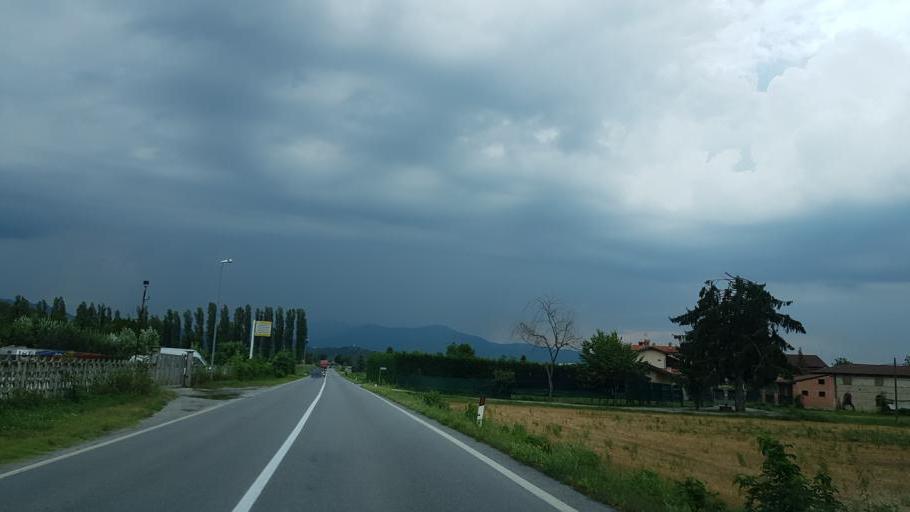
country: IT
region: Piedmont
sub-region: Provincia di Cuneo
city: San Rocco
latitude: 44.3941
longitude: 7.4559
